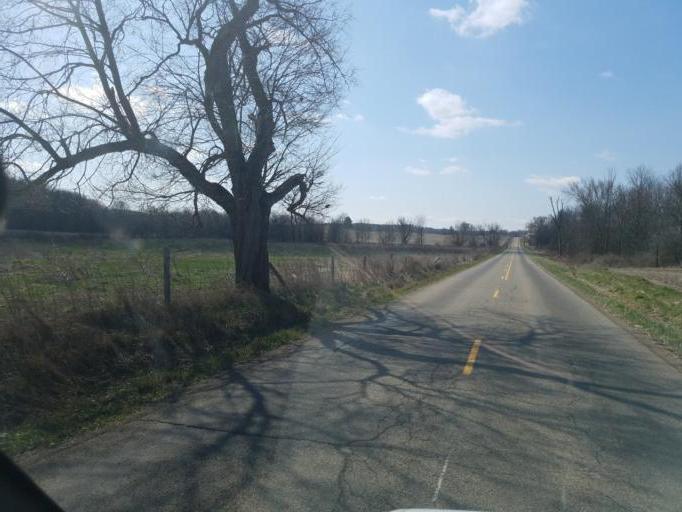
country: US
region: Ohio
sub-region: Knox County
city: Oak Hill
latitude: 40.2932
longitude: -82.2837
